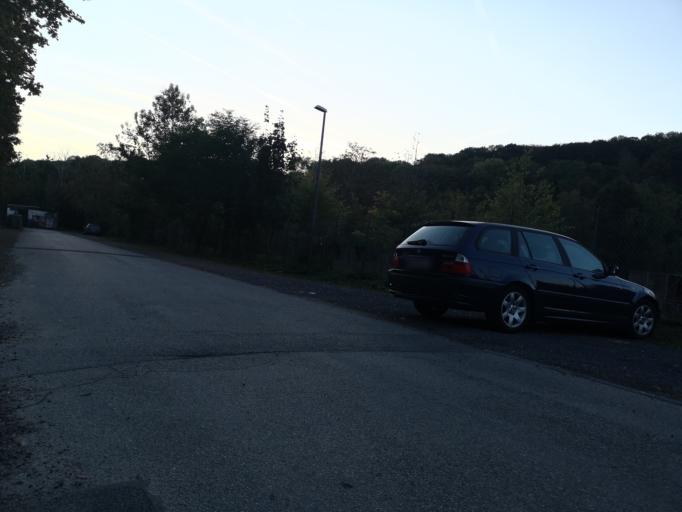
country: DE
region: North Rhine-Westphalia
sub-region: Regierungsbezirk Koln
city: Kreuzau
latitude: 50.7452
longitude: 6.4837
